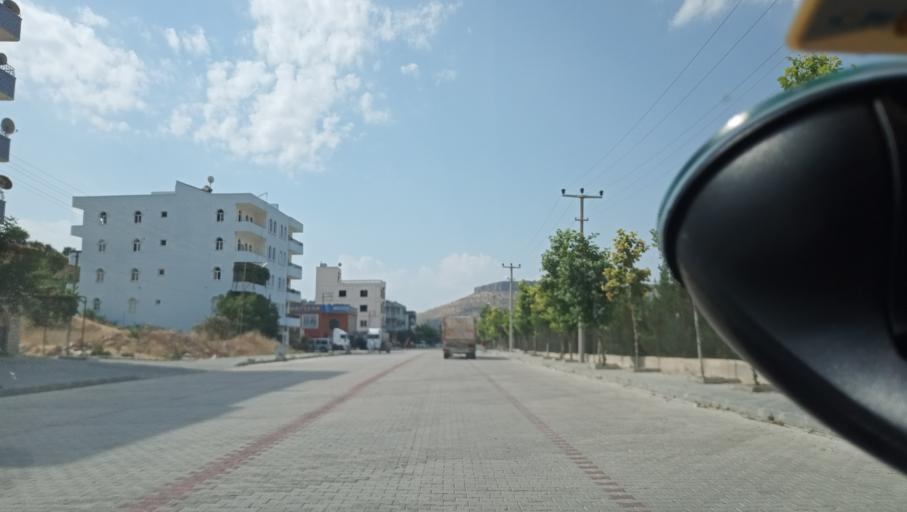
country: TR
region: Mardin
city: Kabala
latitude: 37.3465
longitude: 40.8038
